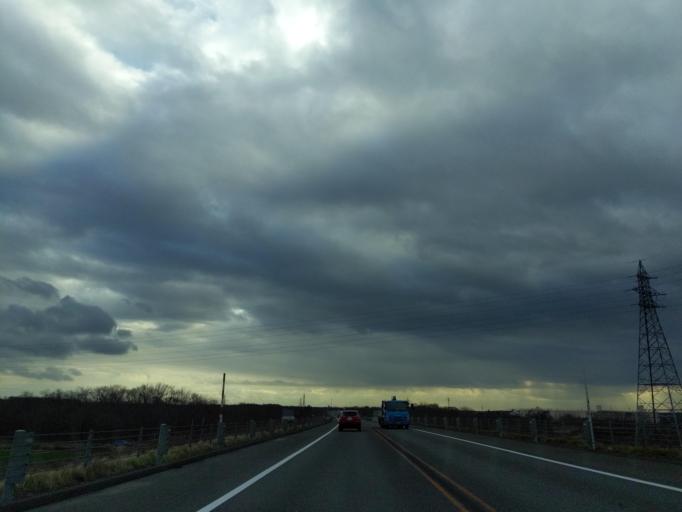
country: JP
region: Hokkaido
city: Chitose
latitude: 42.8384
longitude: 141.6928
